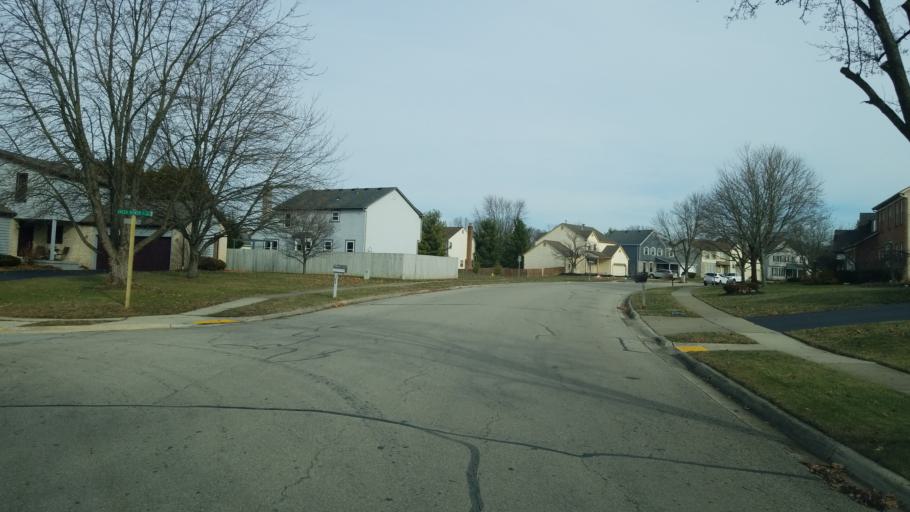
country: US
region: Ohio
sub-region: Delaware County
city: Lewis Center
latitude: 40.1605
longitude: -83.0281
